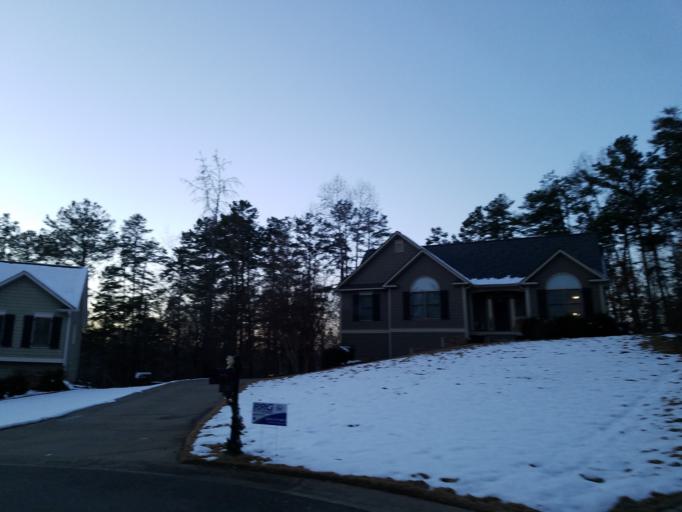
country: US
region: Georgia
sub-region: Pickens County
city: Nelson
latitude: 34.3905
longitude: -84.3725
